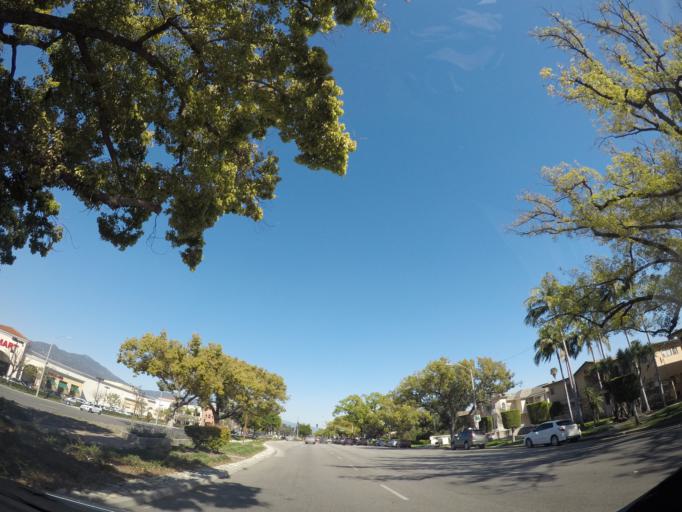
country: US
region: California
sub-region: Los Angeles County
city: Temple City
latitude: 34.1308
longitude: -118.0665
